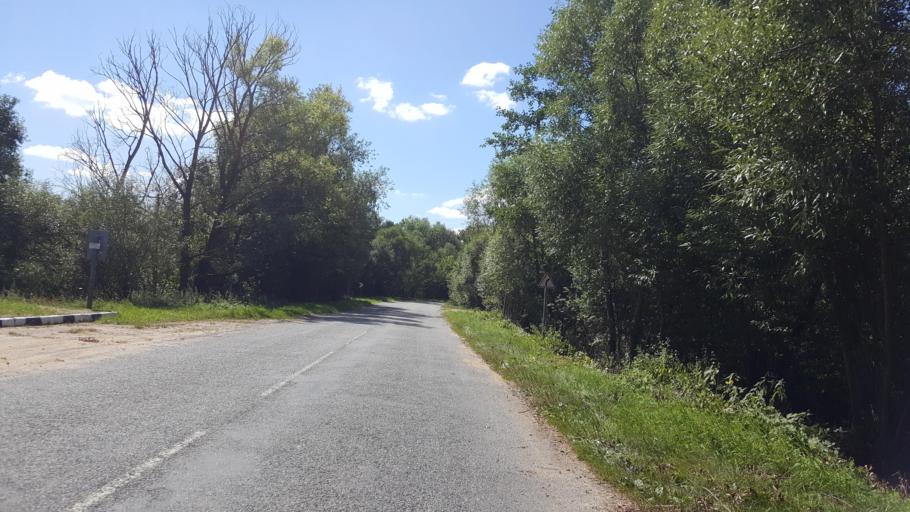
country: BY
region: Brest
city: Horad Kobryn
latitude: 52.2989
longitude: 24.3517
